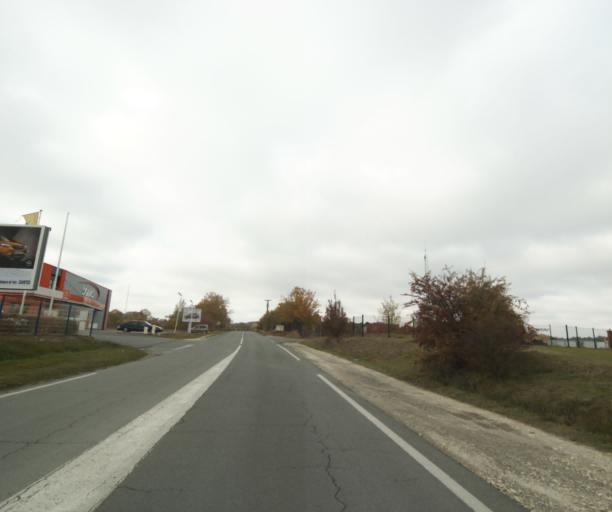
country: FR
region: Poitou-Charentes
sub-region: Departement de la Charente-Maritime
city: Saintes
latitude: 45.7503
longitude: -0.6692
